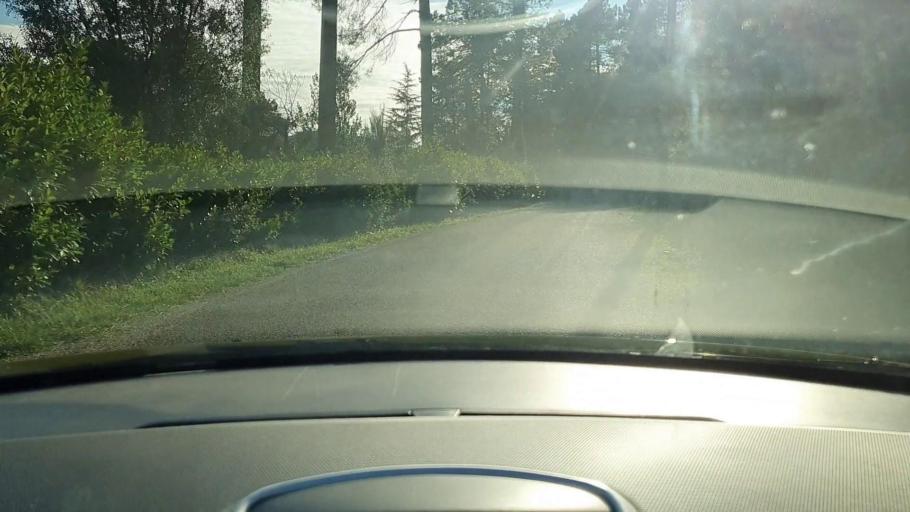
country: FR
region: Languedoc-Roussillon
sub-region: Departement du Gard
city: Branoux-les-Taillades
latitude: 44.2429
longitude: 3.9838
